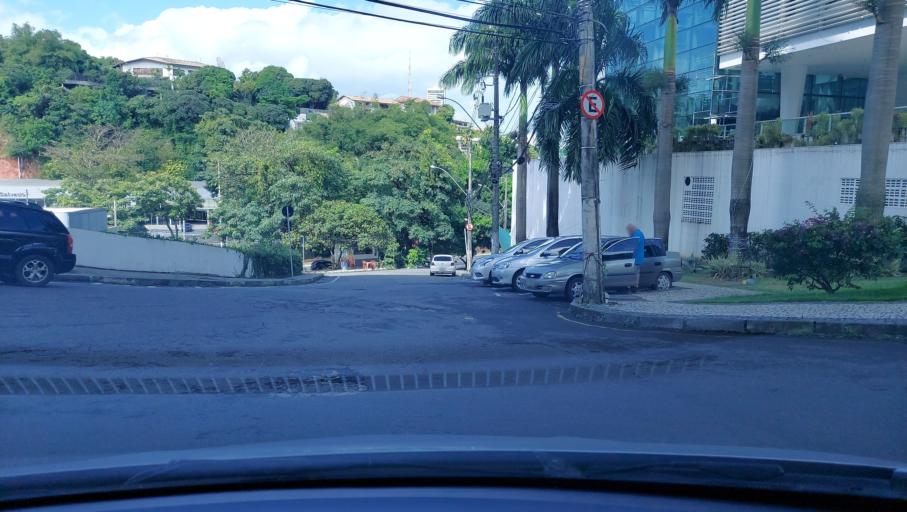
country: BR
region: Bahia
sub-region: Salvador
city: Salvador
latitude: -13.0026
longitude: -38.5022
